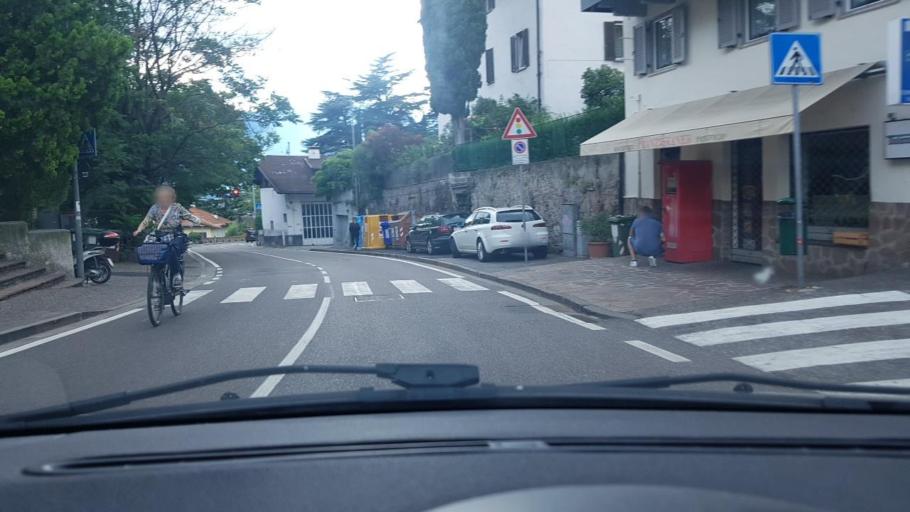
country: IT
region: Trentino-Alto Adige
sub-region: Bolzano
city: Cardano
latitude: 46.4988
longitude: 11.3750
